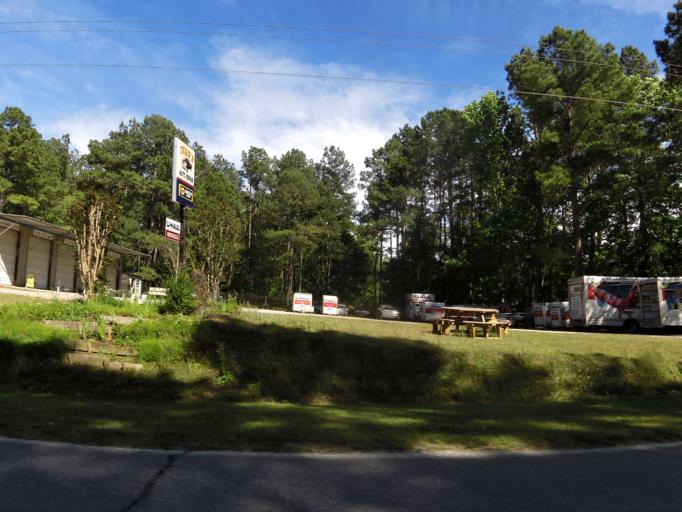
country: US
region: South Carolina
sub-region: Bamberg County
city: Denmark
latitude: 33.2494
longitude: -81.1634
